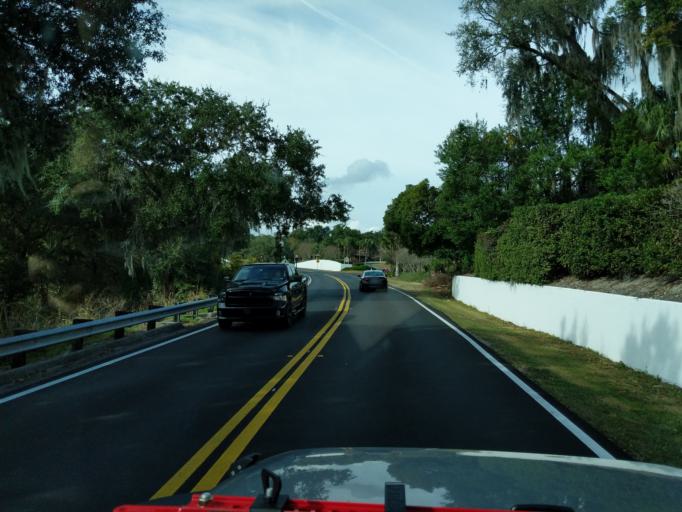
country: US
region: Florida
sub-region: Lake County
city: Mount Dora
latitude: 28.8023
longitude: -81.6485
